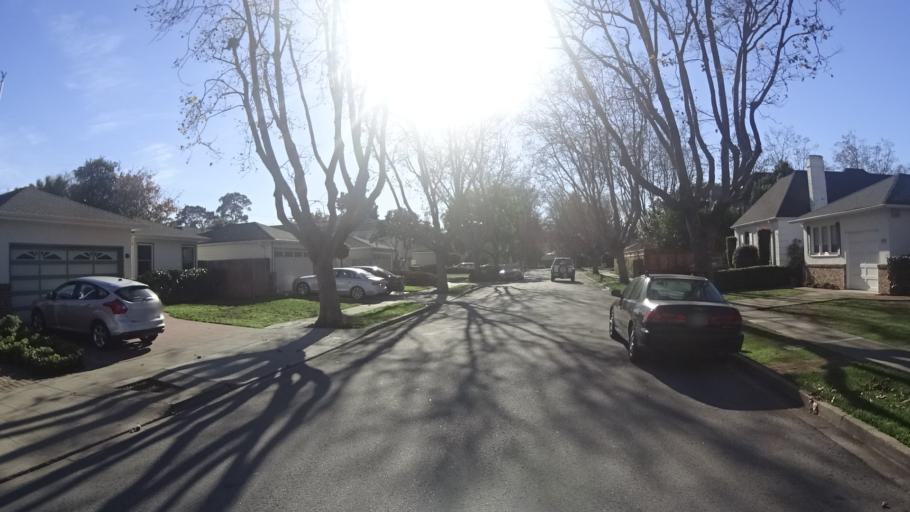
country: US
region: California
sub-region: San Mateo County
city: Burlingame
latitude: 37.5850
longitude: -122.3433
